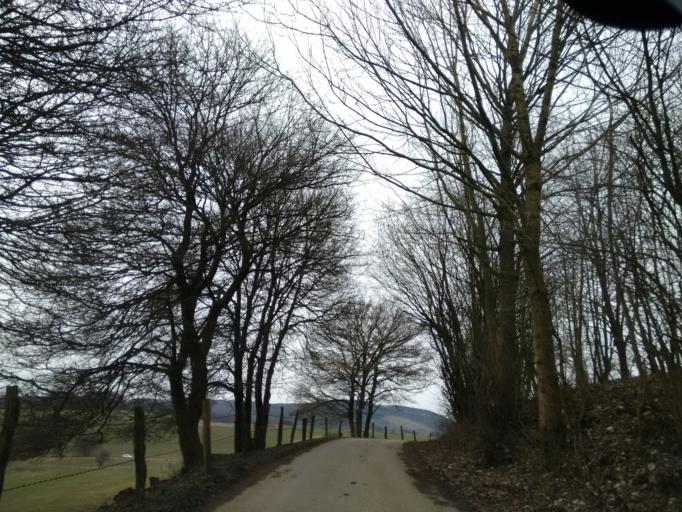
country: DE
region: North Rhine-Westphalia
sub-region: Regierungsbezirk Detmold
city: Bad Driburg
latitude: 51.6863
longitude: 9.0007
